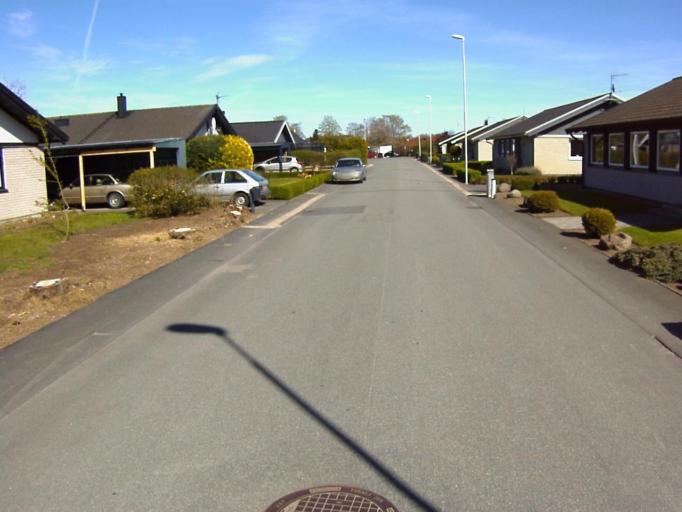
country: SE
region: Skane
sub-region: Kristianstads Kommun
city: Kristianstad
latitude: 56.0097
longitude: 14.1431
